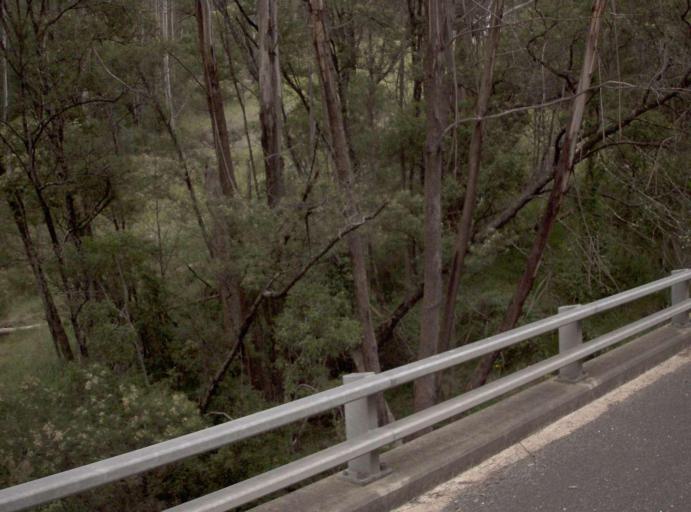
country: AU
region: New South Wales
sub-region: Bombala
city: Bombala
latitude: -37.3323
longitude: 149.2057
